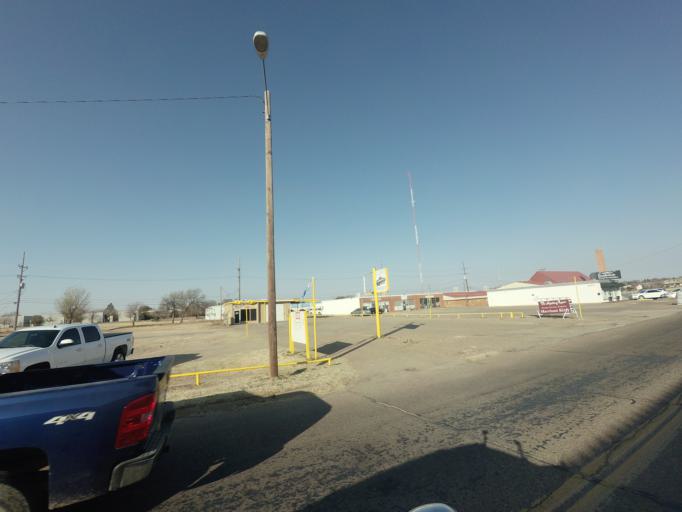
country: US
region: New Mexico
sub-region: Curry County
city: Clovis
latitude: 34.4143
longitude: -103.2053
